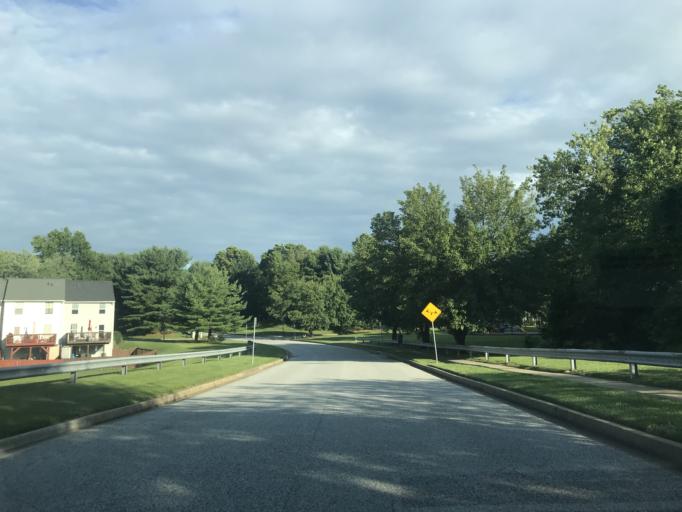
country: US
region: Maryland
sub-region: Harford County
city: South Bel Air
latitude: 39.5616
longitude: -76.3257
